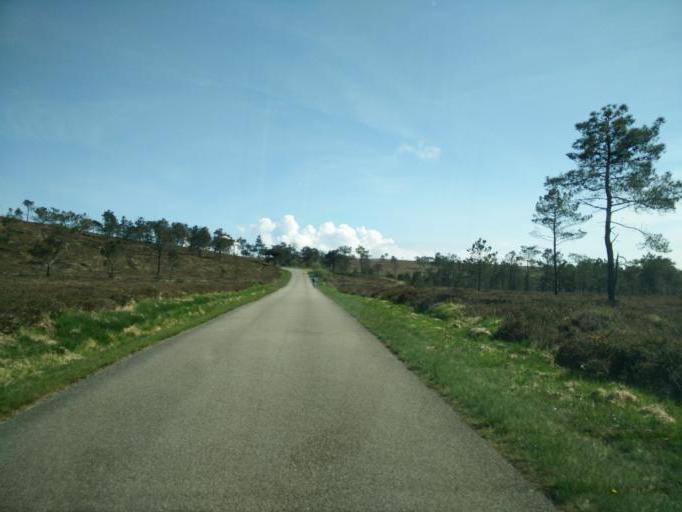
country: FR
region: Brittany
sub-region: Departement du Finistere
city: Plomodiern
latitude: 48.2087
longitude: -4.2446
